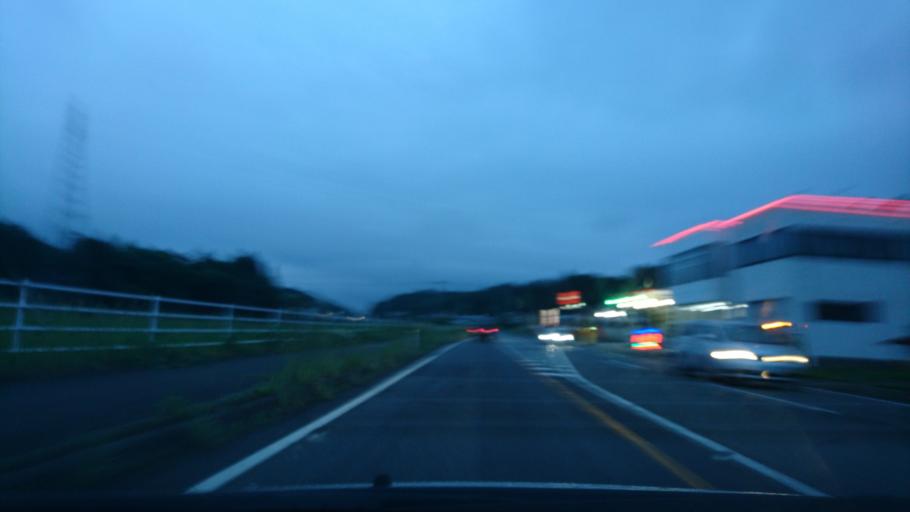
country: JP
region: Iwate
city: Ichinoseki
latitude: 38.7935
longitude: 141.0523
